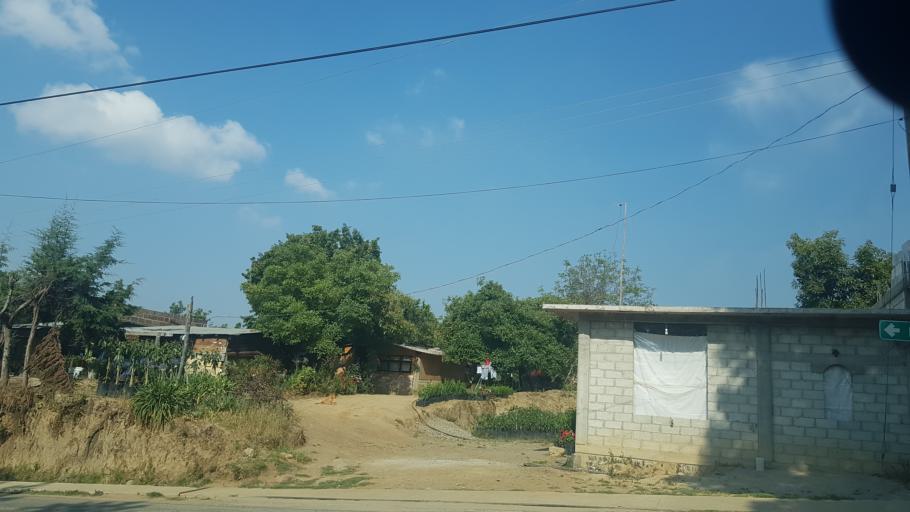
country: MX
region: Morelos
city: Hueyapan
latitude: 18.8929
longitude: -98.6774
